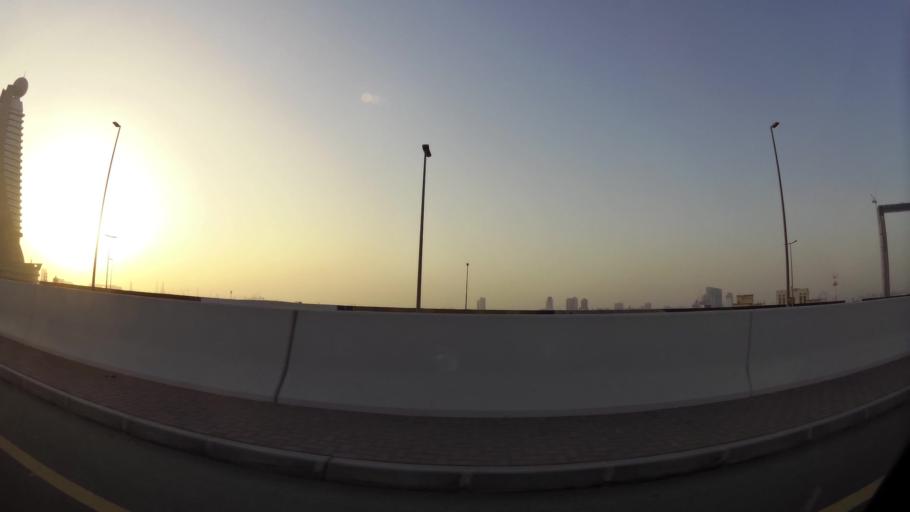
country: AE
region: Ash Shariqah
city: Sharjah
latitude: 25.2306
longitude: 55.2958
